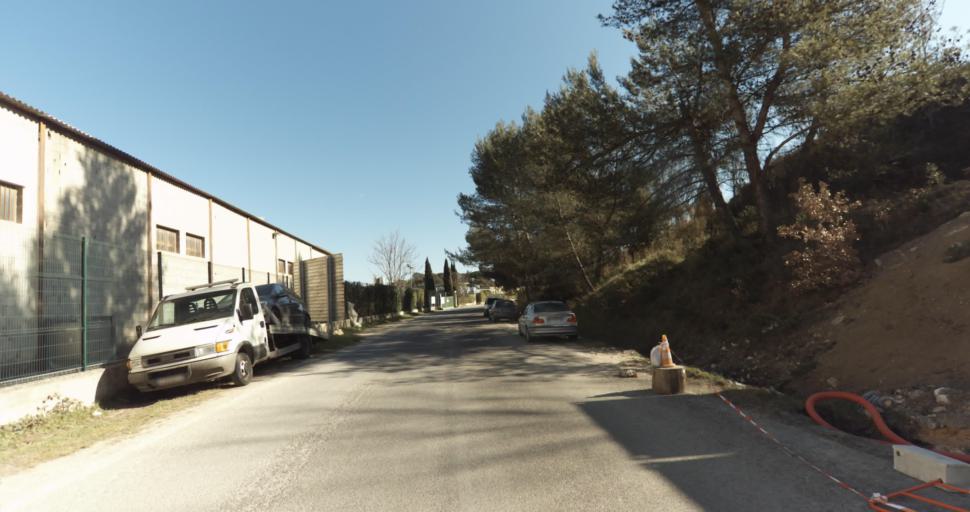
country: FR
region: Provence-Alpes-Cote d'Azur
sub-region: Departement des Bouches-du-Rhone
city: Cadolive
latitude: 43.3998
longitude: 5.5601
